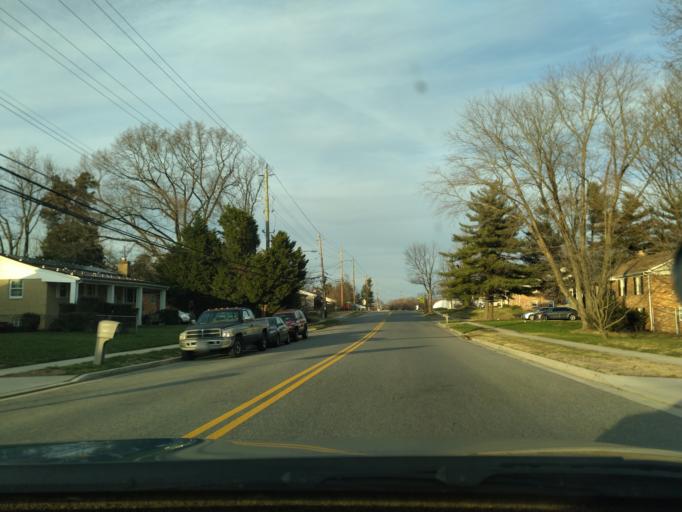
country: US
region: Maryland
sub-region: Prince George's County
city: Clinton
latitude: 38.7457
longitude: -76.9015
